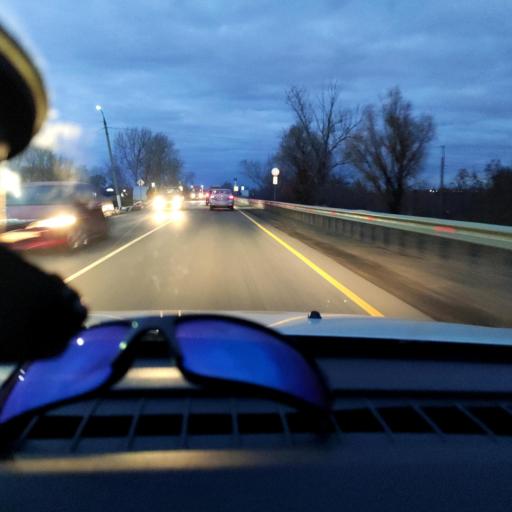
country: RU
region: Samara
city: Samara
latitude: 53.1161
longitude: 50.1243
